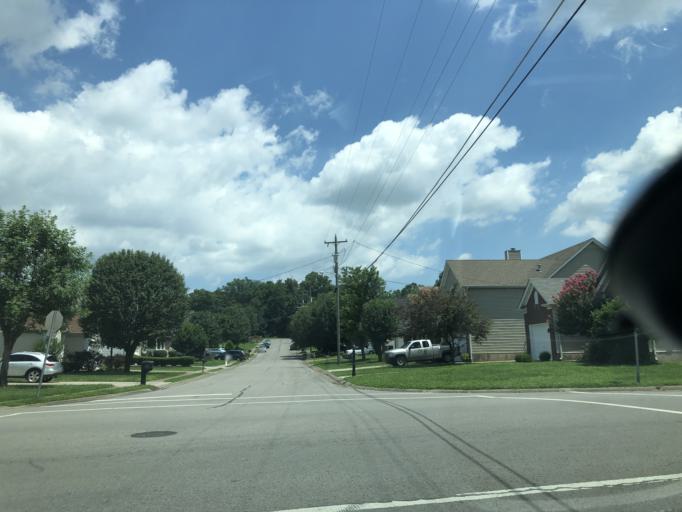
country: US
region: Tennessee
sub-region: Rutherford County
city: La Vergne
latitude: 36.0424
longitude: -86.6237
